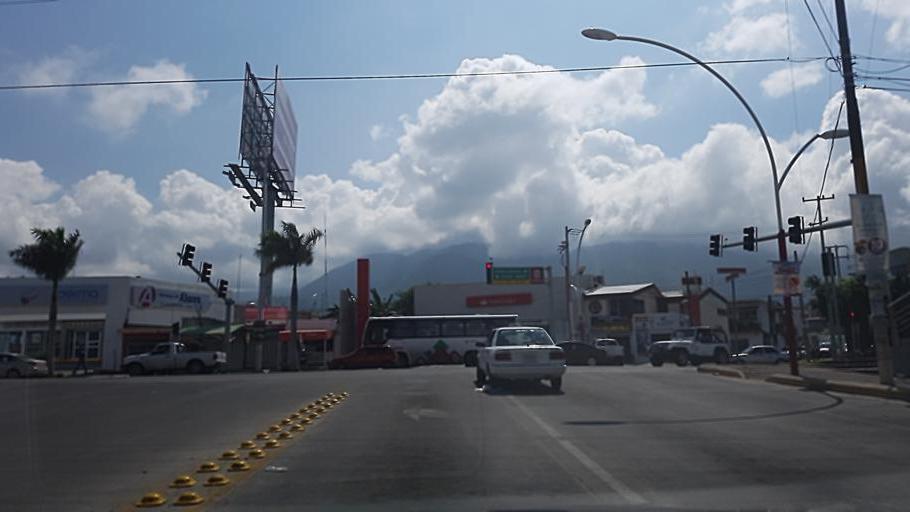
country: MX
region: Nayarit
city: Tepic
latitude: 21.4889
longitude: -104.8943
